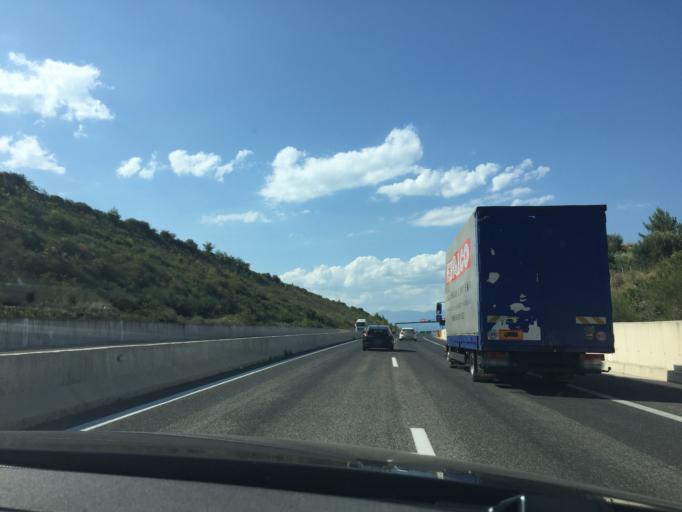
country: GR
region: Central Greece
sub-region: Nomos Fthiotidos
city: Ayios Konstandinos
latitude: 38.7562
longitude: 22.8448
